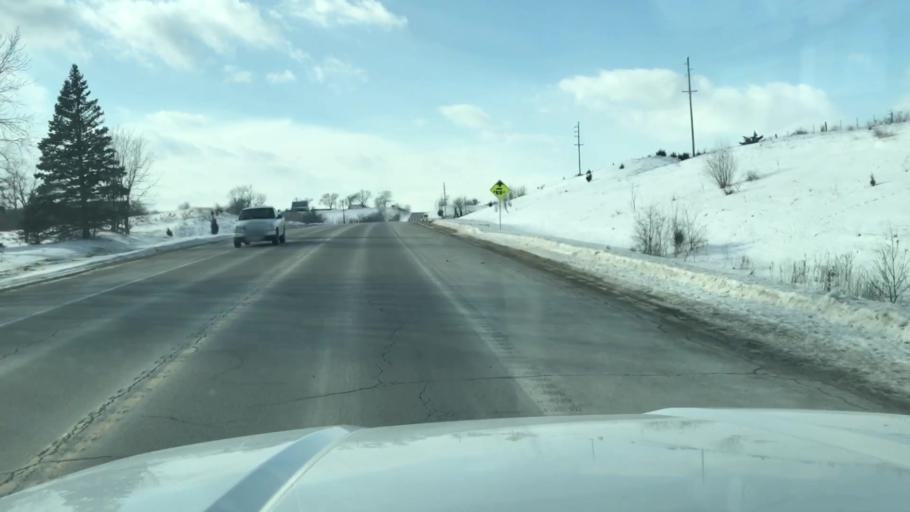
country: US
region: Missouri
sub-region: Nodaway County
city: Maryville
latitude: 40.3436
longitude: -94.6946
